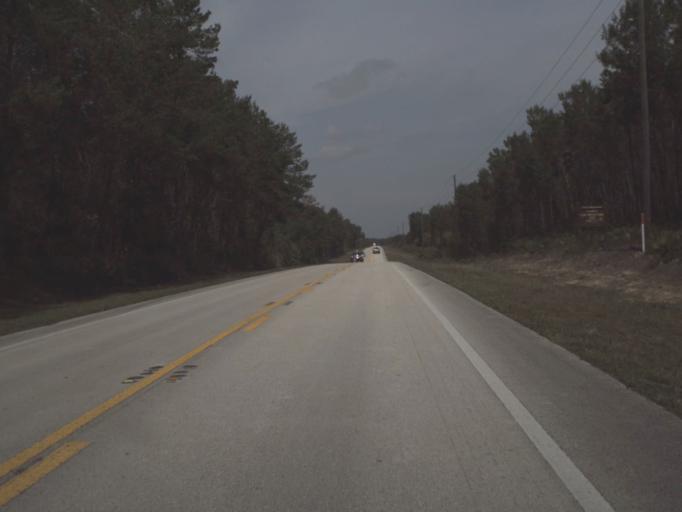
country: US
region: Florida
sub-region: Putnam County
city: Crescent City
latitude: 29.3201
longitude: -81.6987
